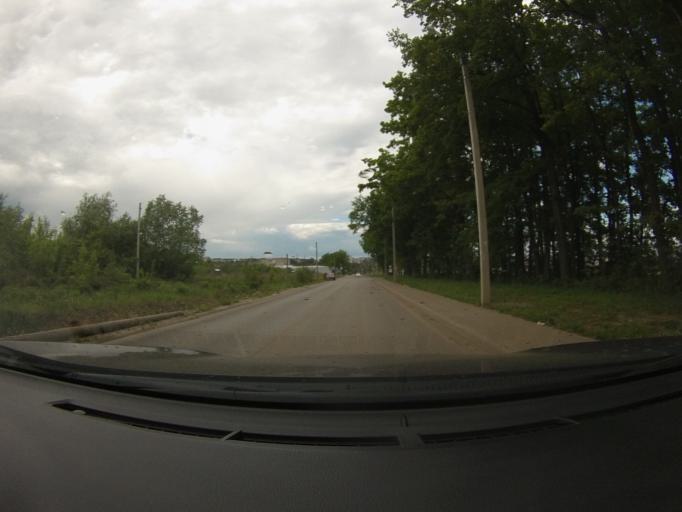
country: RU
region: Tula
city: Tula
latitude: 54.1737
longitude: 37.6486
